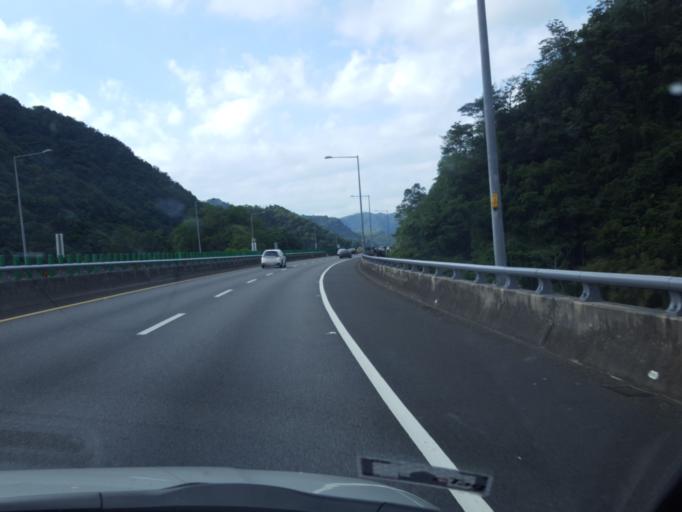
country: TW
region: Taipei
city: Taipei
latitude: 24.9833
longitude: 121.6618
